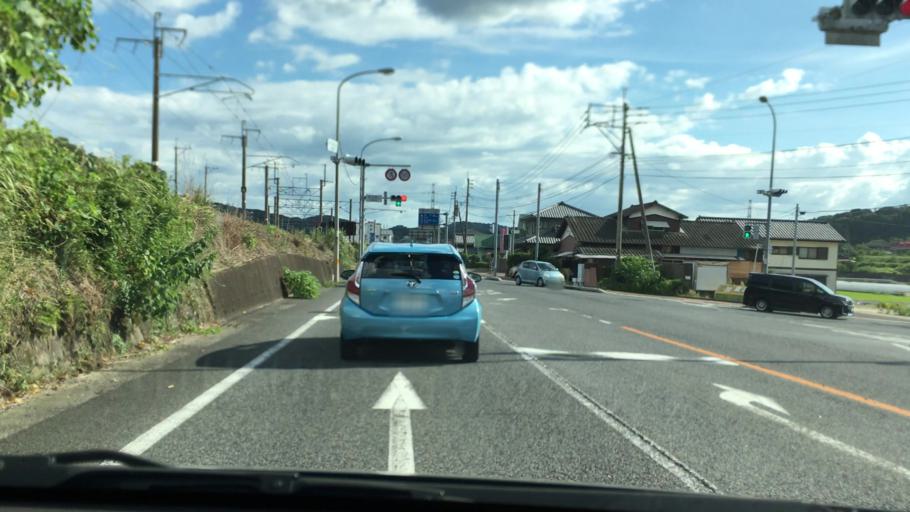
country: JP
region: Saga Prefecture
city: Imaricho-ko
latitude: 33.1852
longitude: 129.8547
